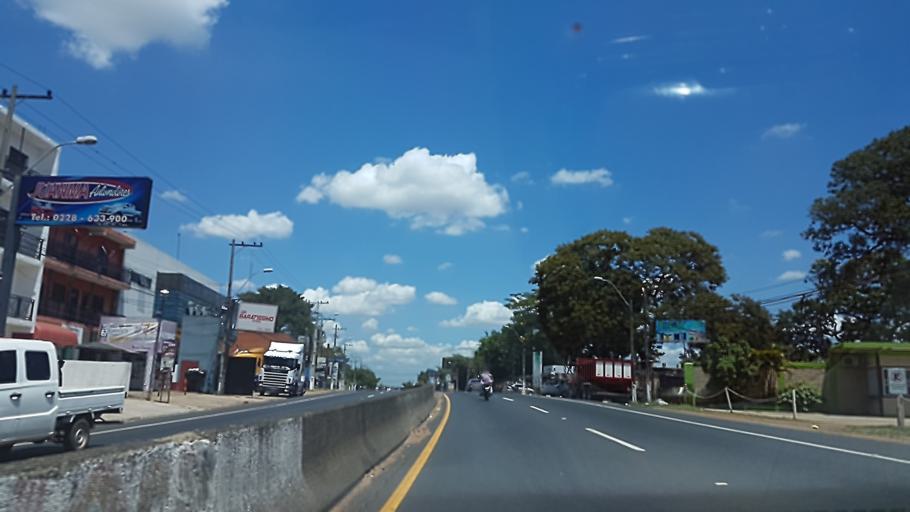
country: PY
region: Central
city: Capiata
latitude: -25.3501
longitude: -57.4493
